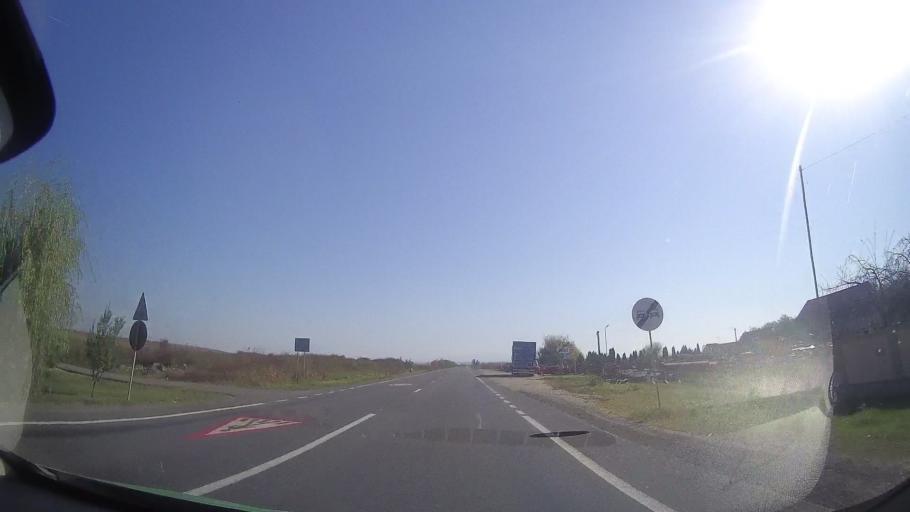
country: RO
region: Timis
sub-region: Comuna Belint
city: Belint
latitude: 45.7478
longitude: 21.7825
